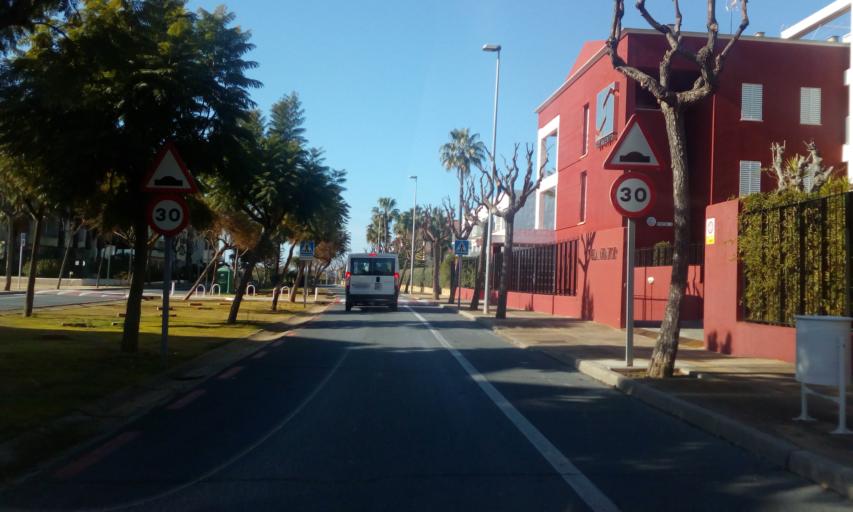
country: ES
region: Andalusia
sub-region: Provincia de Huelva
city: Lepe
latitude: 37.2063
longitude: -7.2415
